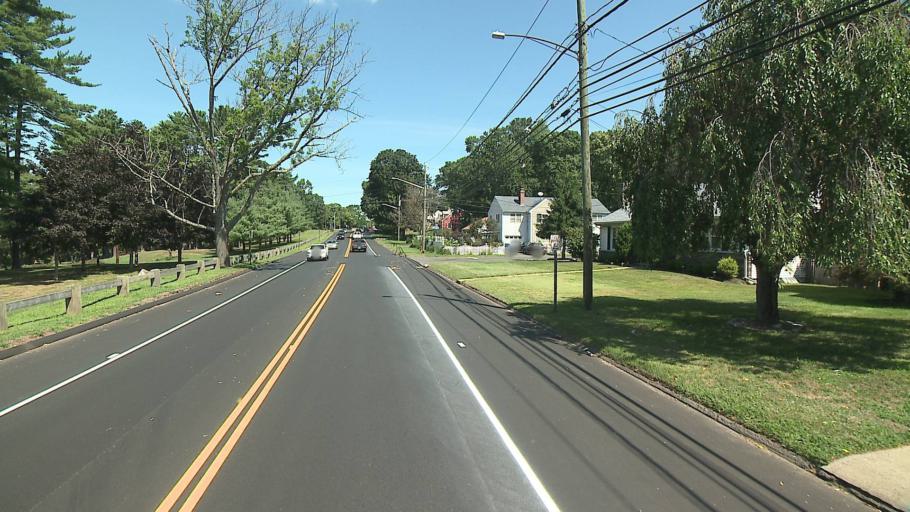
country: US
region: Connecticut
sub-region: Fairfield County
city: Trumbull
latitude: 41.2203
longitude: -73.1767
